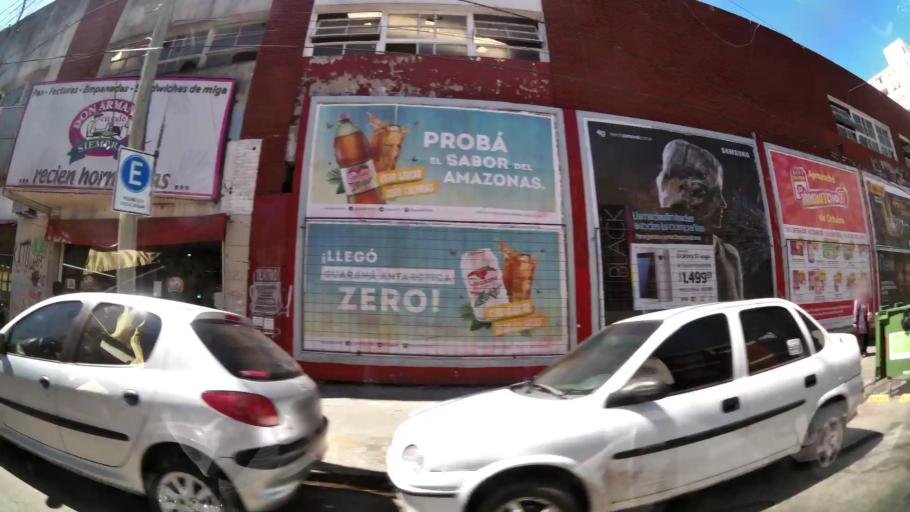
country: AR
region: Buenos Aires
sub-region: Partido de Vicente Lopez
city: Olivos
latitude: -34.5245
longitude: -58.4850
